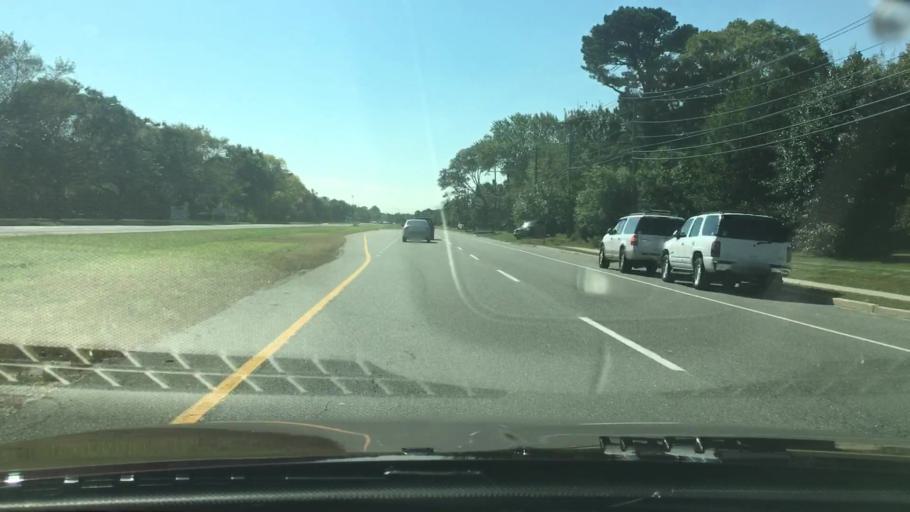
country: US
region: New York
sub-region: Suffolk County
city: Yaphank
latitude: 40.8159
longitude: -72.9495
